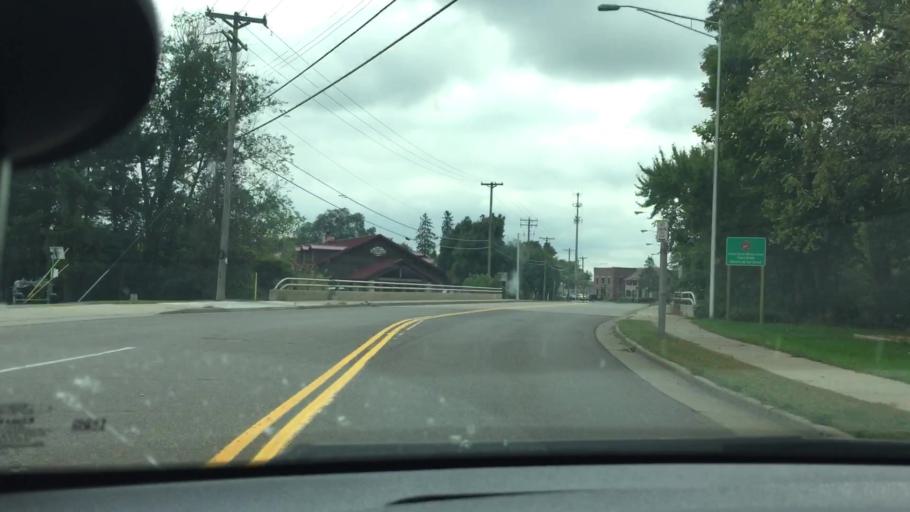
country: US
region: Wisconsin
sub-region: Chippewa County
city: Chippewa Falls
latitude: 44.9444
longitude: -91.3964
